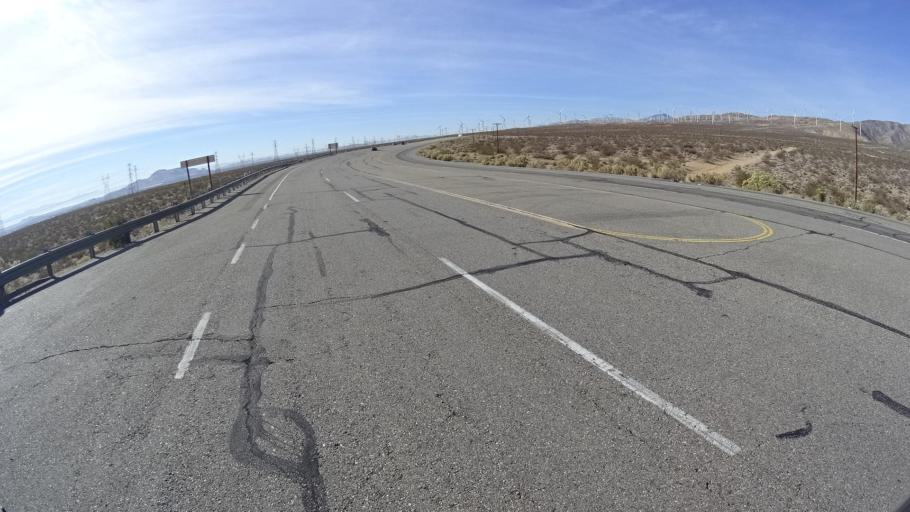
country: US
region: California
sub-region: Kern County
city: Mojave
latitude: 35.1096
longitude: -118.1810
